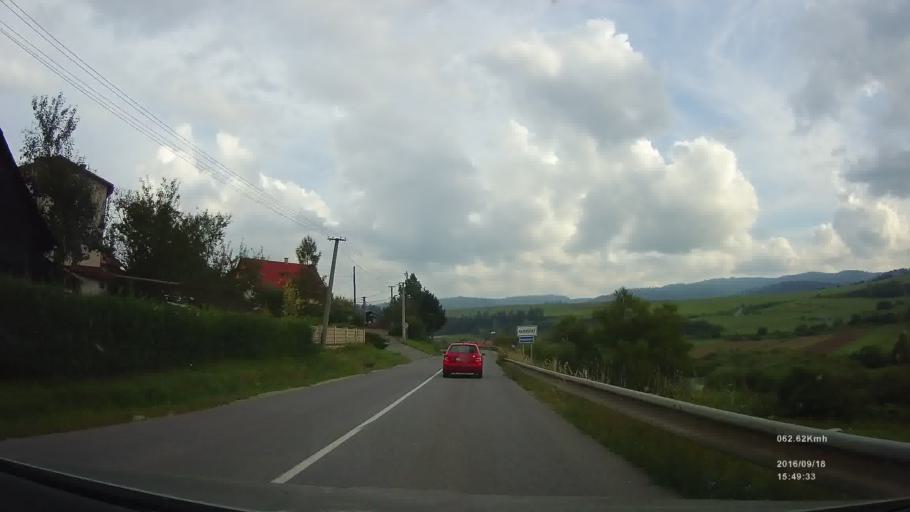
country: SK
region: Kosicky
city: Spisska Nova Ves
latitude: 48.9165
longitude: 20.6105
